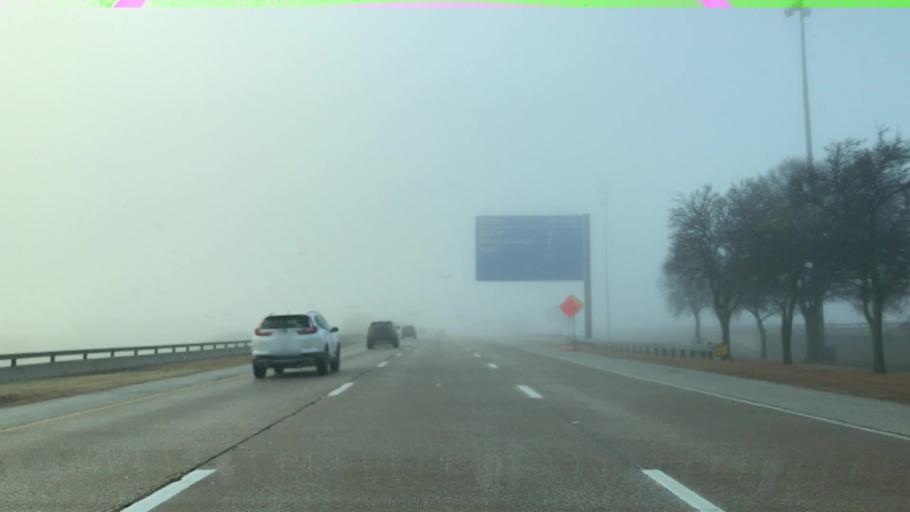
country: US
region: Texas
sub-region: Tarrant County
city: Grapevine
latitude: 32.9162
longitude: -97.0410
